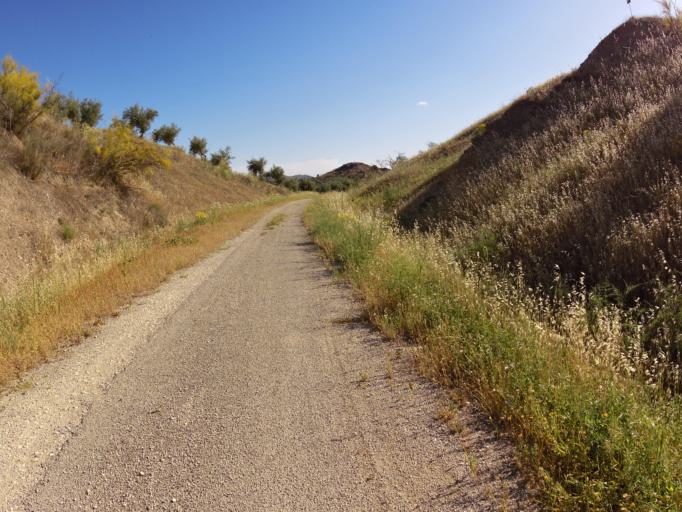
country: ES
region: Andalusia
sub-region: Province of Cordoba
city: Fuente-Tojar
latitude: 37.5842
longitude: -4.1762
